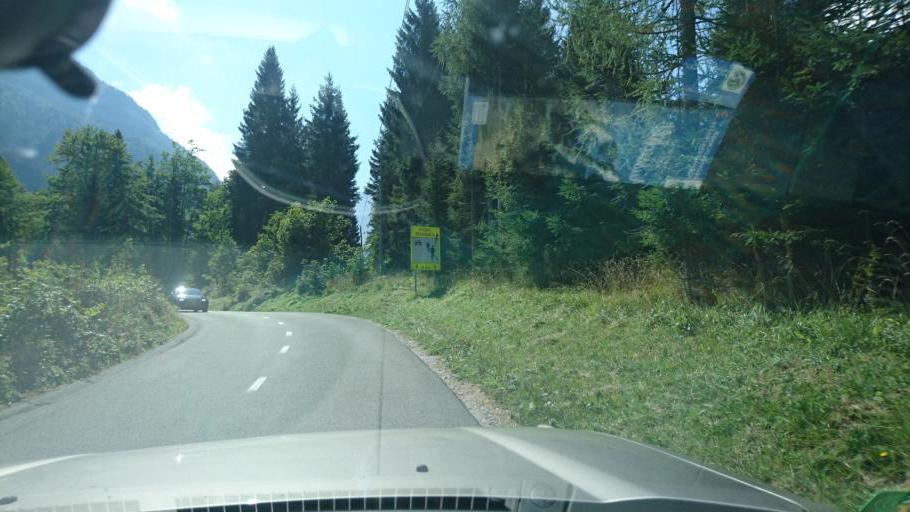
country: SI
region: Kranjska Gora
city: Kranjska Gora
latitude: 46.4649
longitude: 13.7815
